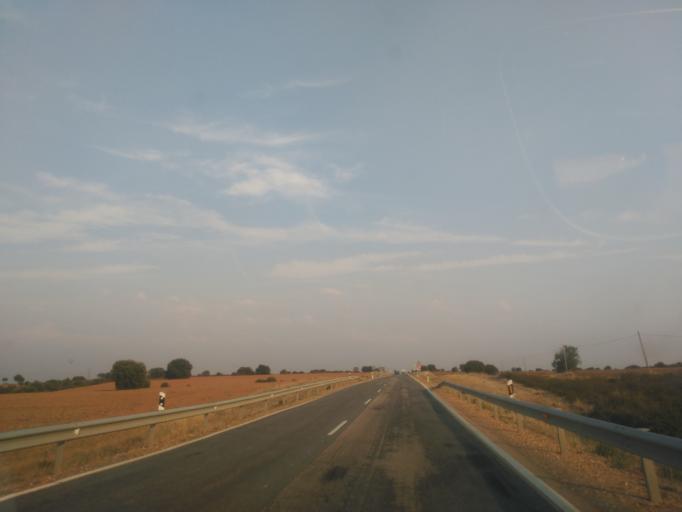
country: ES
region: Castille and Leon
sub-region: Provincia de Zamora
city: Perilla de Castro
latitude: 41.7386
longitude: -5.8312
